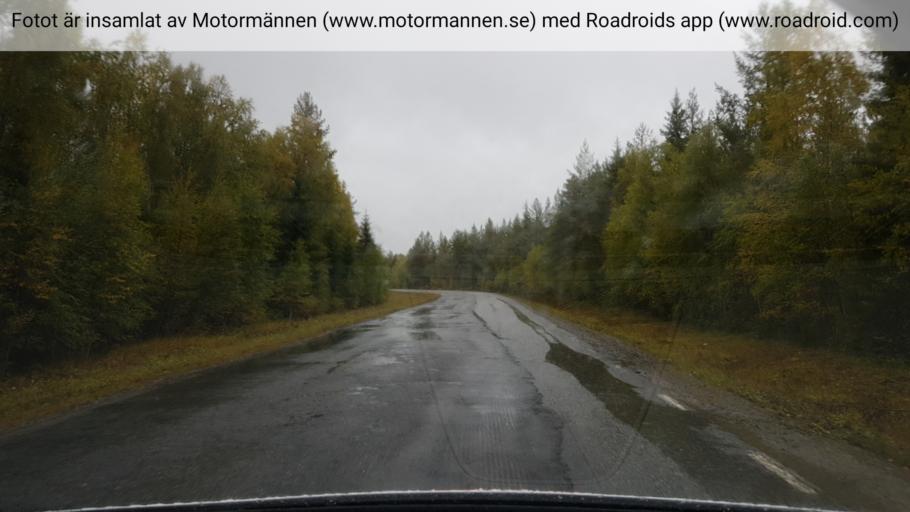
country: SE
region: Vaesterbotten
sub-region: Vannas Kommun
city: Vannasby
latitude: 64.0327
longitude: 19.9328
